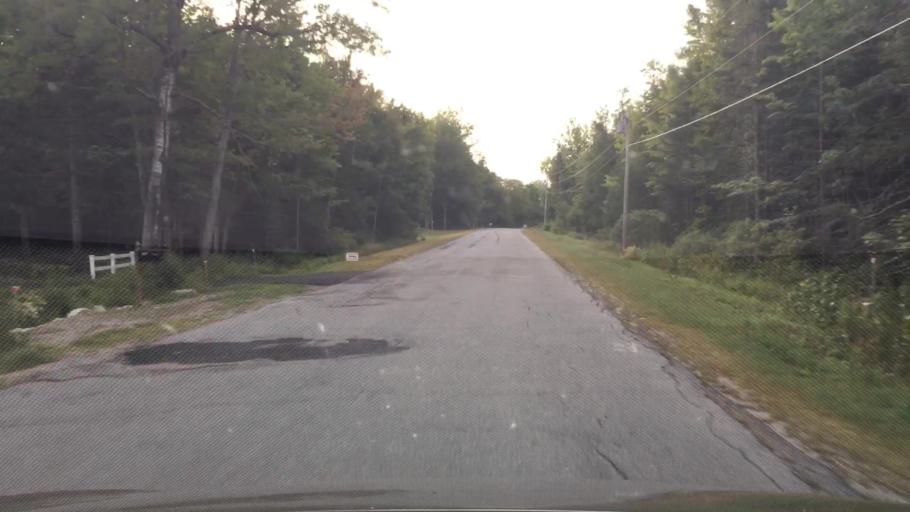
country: US
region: Maine
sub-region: Waldo County
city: Stockton Springs
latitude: 44.4933
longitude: -68.8717
